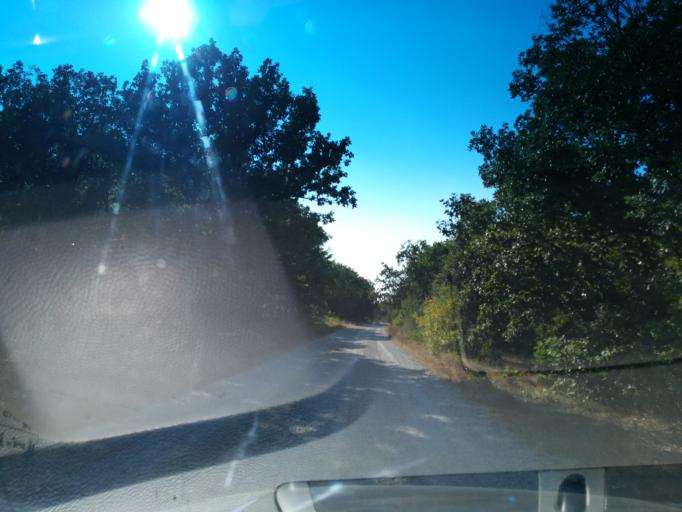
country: BG
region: Khaskovo
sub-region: Obshtina Mineralni Bani
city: Mineralni Bani
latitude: 41.9712
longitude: 25.3256
